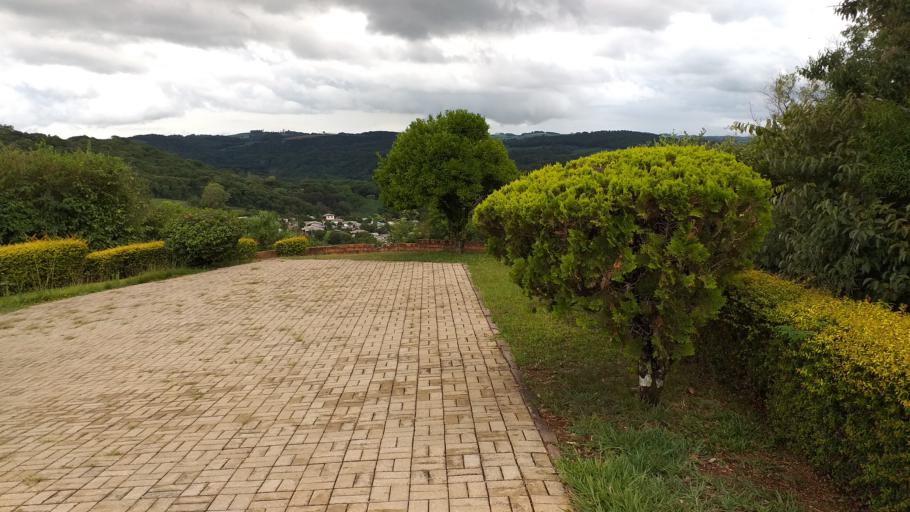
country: BR
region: Rio Grande do Sul
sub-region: Marau
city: Marau
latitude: -28.4428
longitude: -52.1888
